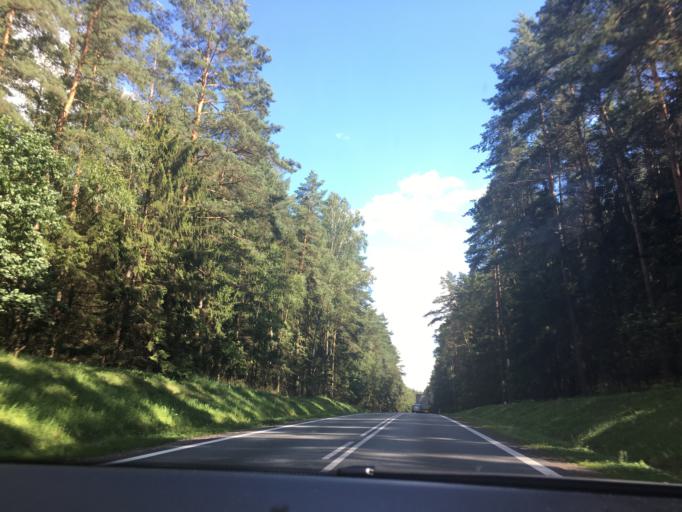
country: PL
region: Podlasie
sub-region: Powiat bialostocki
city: Wasilkow
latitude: 53.2592
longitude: 23.1386
